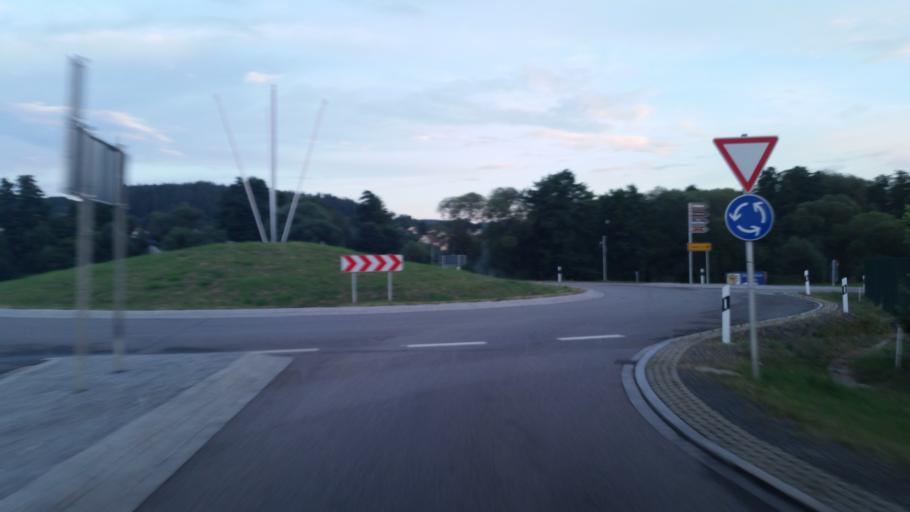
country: DE
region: Bavaria
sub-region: Upper Palatinate
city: Luhe-Wildenau
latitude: 49.5890
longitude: 12.1474
